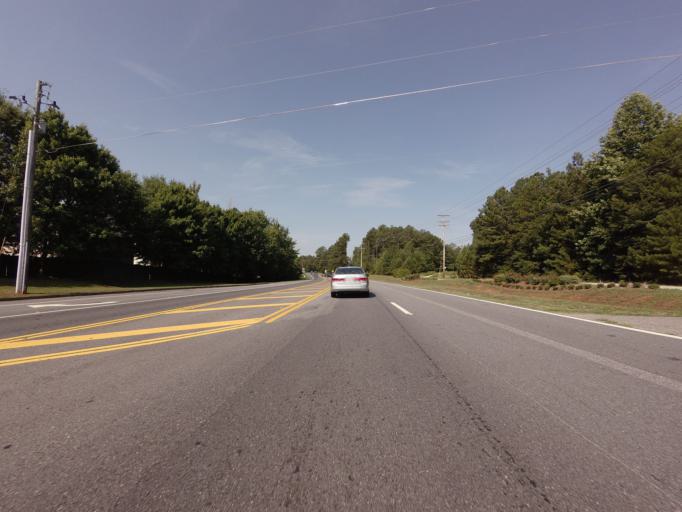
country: US
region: Georgia
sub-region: Fulton County
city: Johns Creek
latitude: 34.0640
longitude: -84.2182
